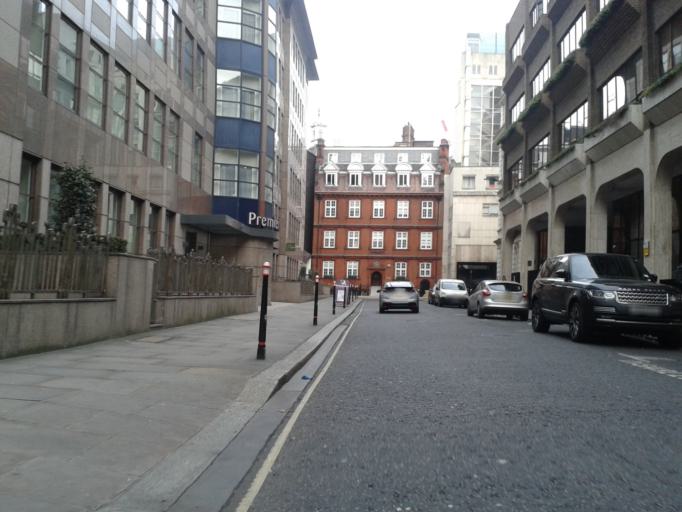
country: GB
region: England
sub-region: Greater London
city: Barbican
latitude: 51.5124
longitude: -0.1049
